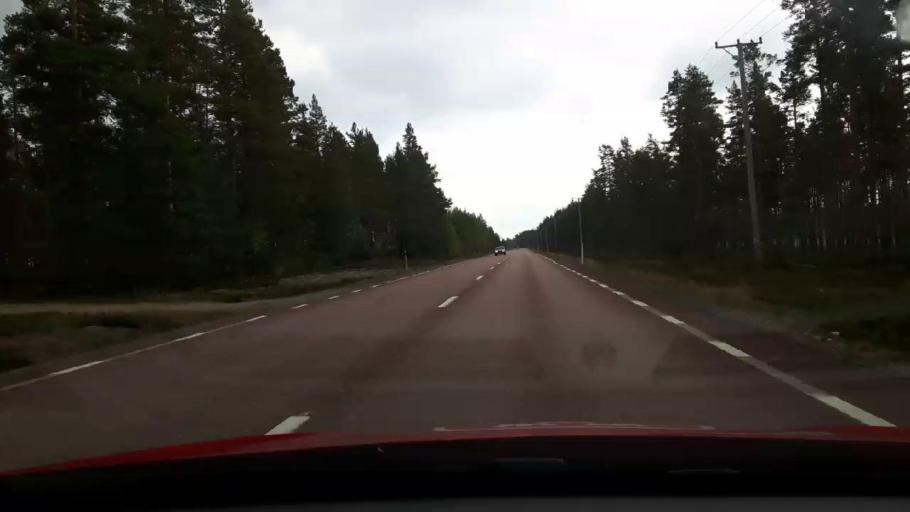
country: SE
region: Gaevleborg
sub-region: Soderhamns Kommun
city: Ljusne
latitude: 61.1053
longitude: 16.9424
